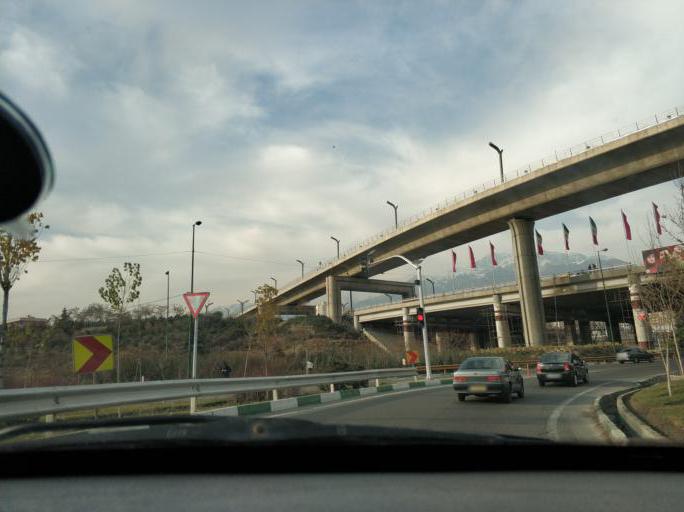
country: IR
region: Tehran
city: Tajrish
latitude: 35.7849
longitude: 51.4920
